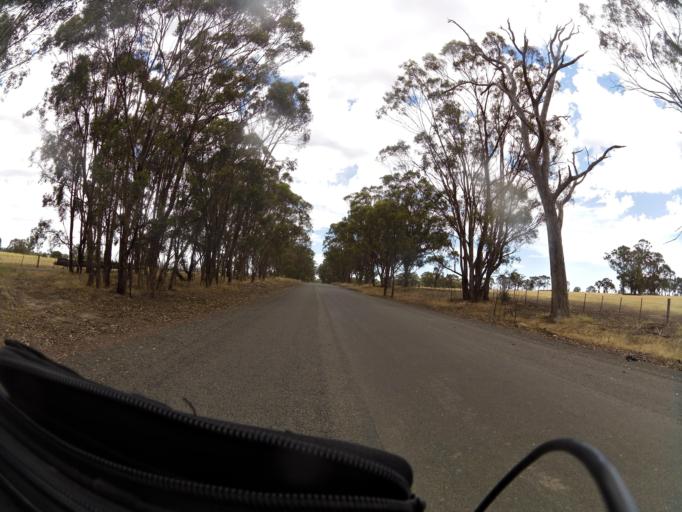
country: AU
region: Victoria
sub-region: Campaspe
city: Kyabram
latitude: -36.7358
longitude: 145.1431
